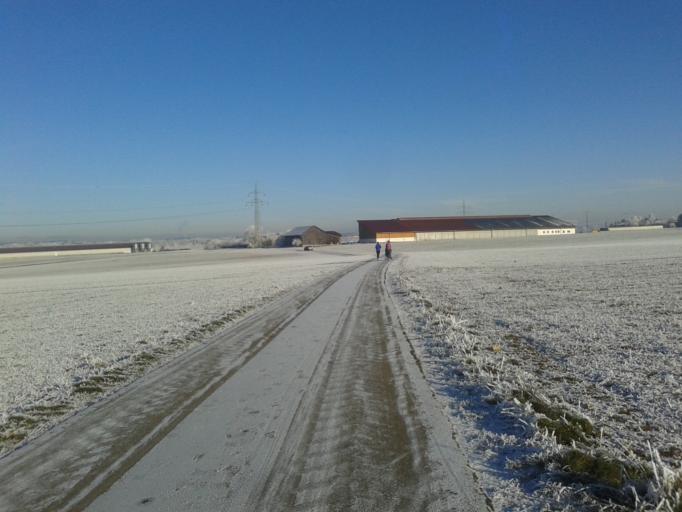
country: DE
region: Baden-Wuerttemberg
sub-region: Tuebingen Region
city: Dornstadt
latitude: 48.4367
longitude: 9.9623
